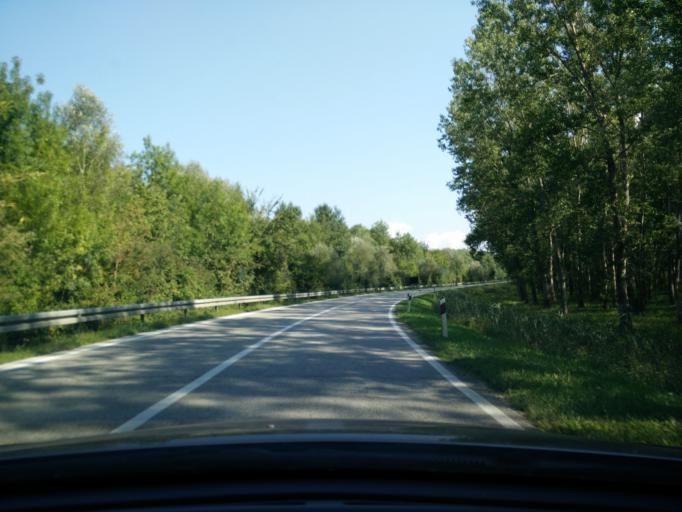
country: HR
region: Istarska
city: Karojba
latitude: 45.3517
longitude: 13.7695
